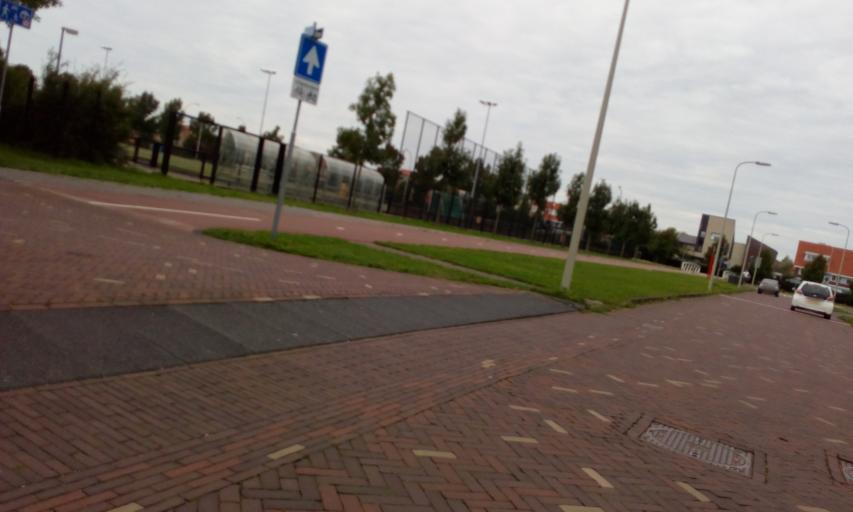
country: NL
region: South Holland
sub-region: Gemeente Den Haag
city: Ypenburg
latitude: 52.0341
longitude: 4.3899
